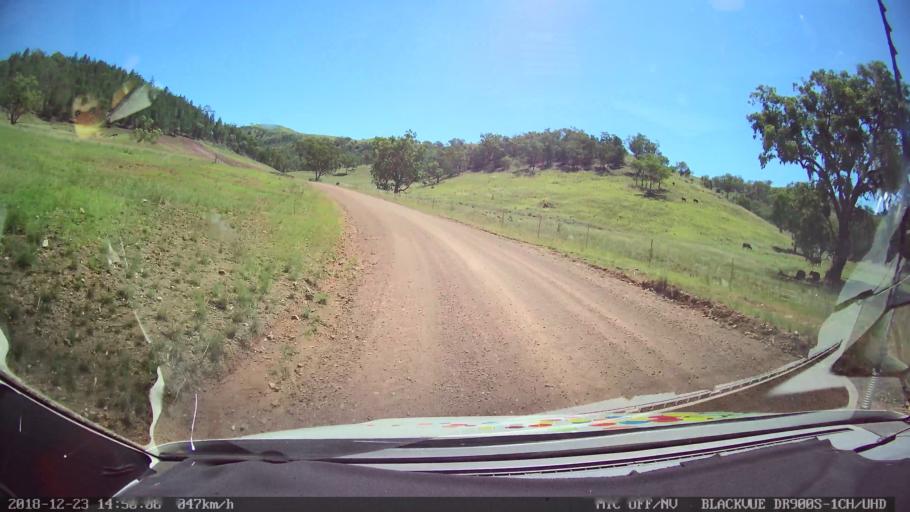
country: AU
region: New South Wales
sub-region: Tamworth Municipality
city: Manilla
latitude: -30.6712
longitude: 150.8589
